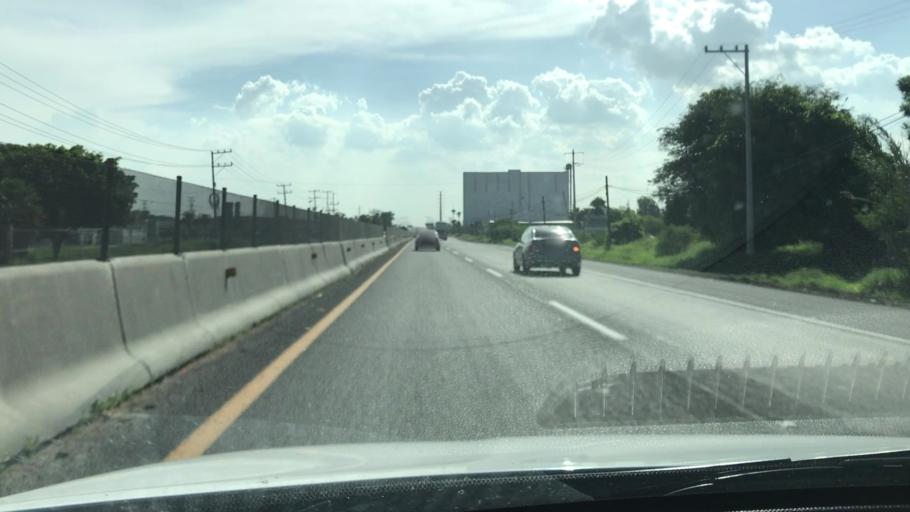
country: MX
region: Guanajuato
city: Villagran
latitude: 20.5092
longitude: -100.9823
